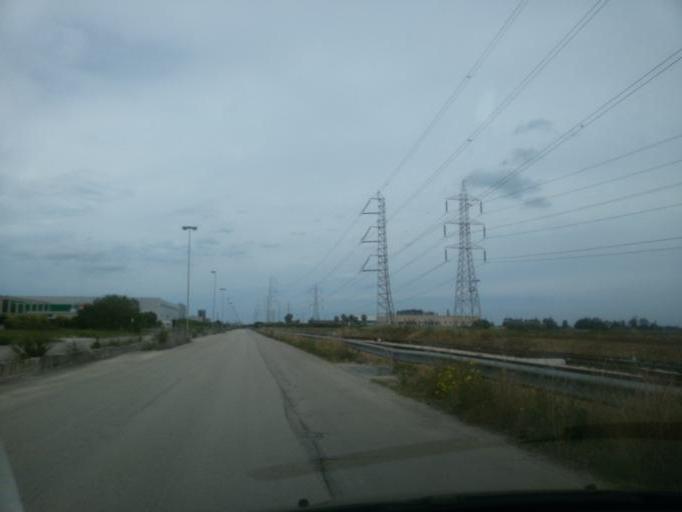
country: IT
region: Apulia
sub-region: Provincia di Brindisi
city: Materdomini
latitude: 40.6281
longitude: 17.9814
